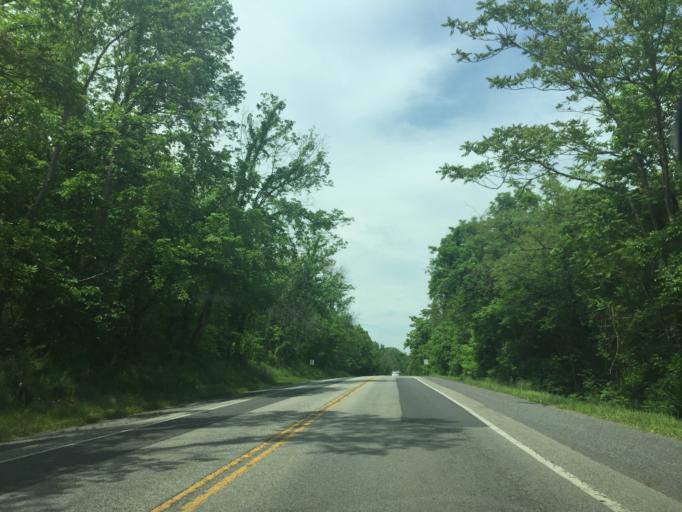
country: US
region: West Virginia
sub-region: Morgan County
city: Berkeley Springs
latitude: 39.6370
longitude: -78.2212
